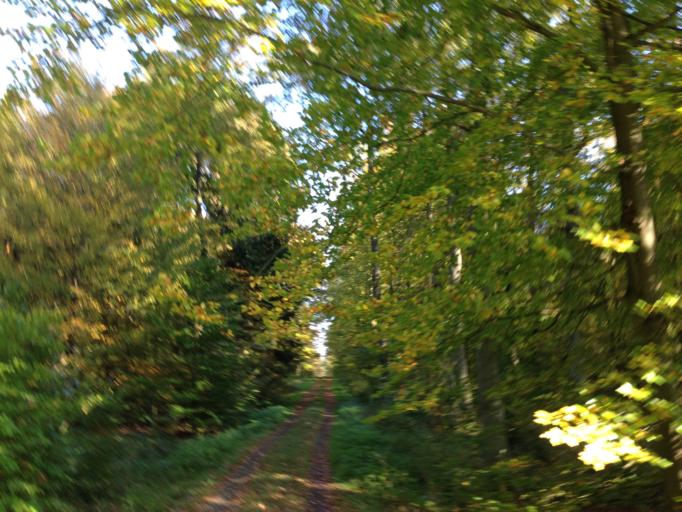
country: DE
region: Hesse
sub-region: Regierungsbezirk Giessen
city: Grossen Buseck
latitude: 50.5700
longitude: 8.7796
